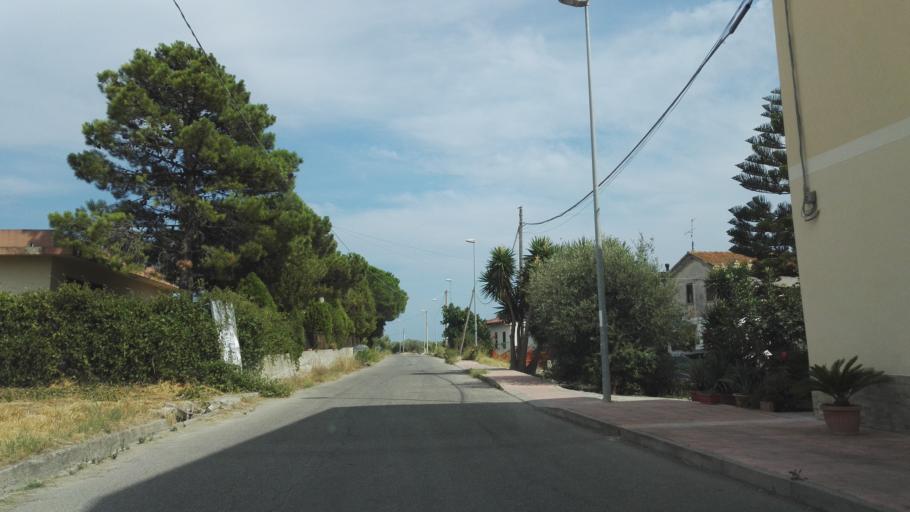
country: IT
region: Calabria
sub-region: Provincia di Reggio Calabria
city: Monasterace Marina
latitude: 38.4269
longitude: 16.5454
